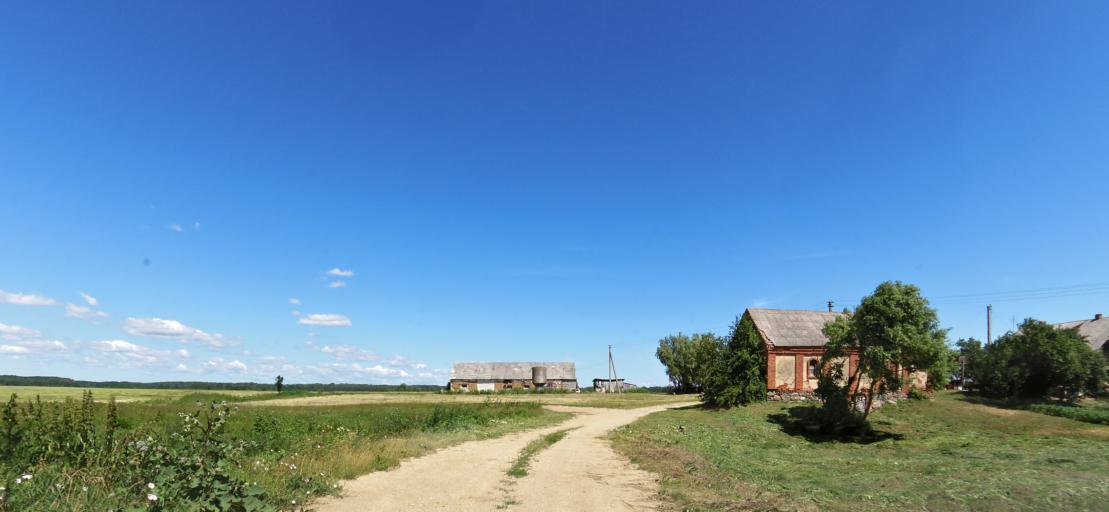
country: LT
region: Panevezys
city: Pasvalys
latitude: 56.2654
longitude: 24.5139
